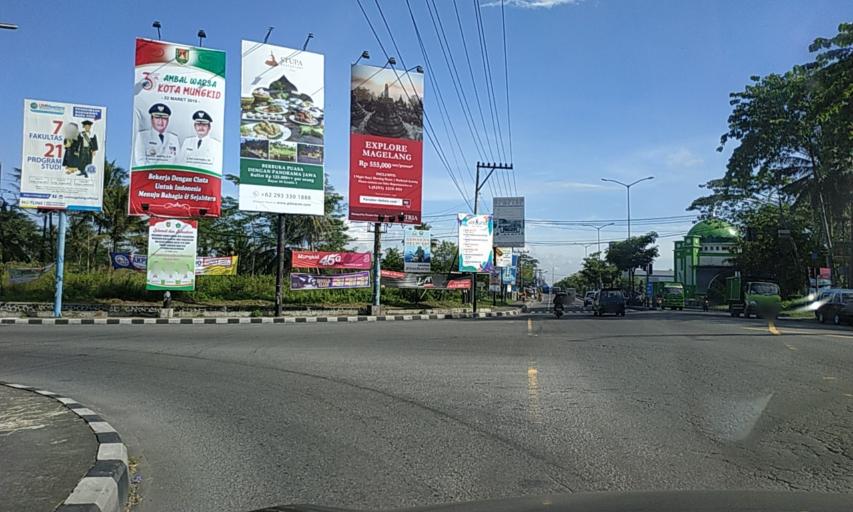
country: ID
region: Central Java
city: Muntilan
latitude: -7.5678
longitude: 110.2589
